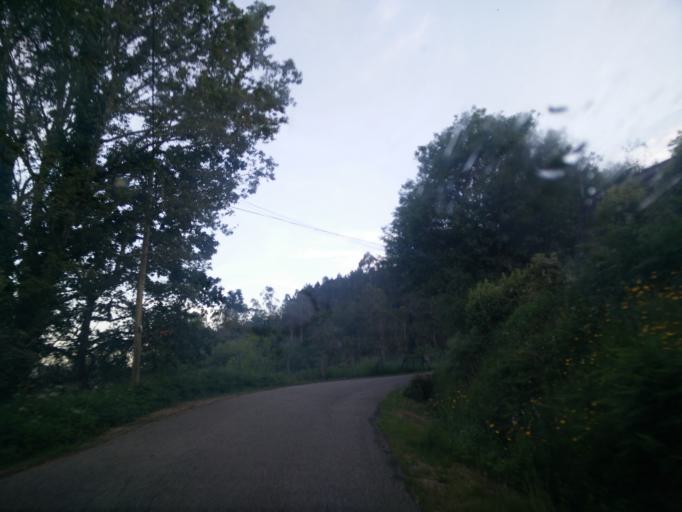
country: ES
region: Galicia
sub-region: Provincia de Pontevedra
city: Mondariz
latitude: 42.2651
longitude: -8.4084
